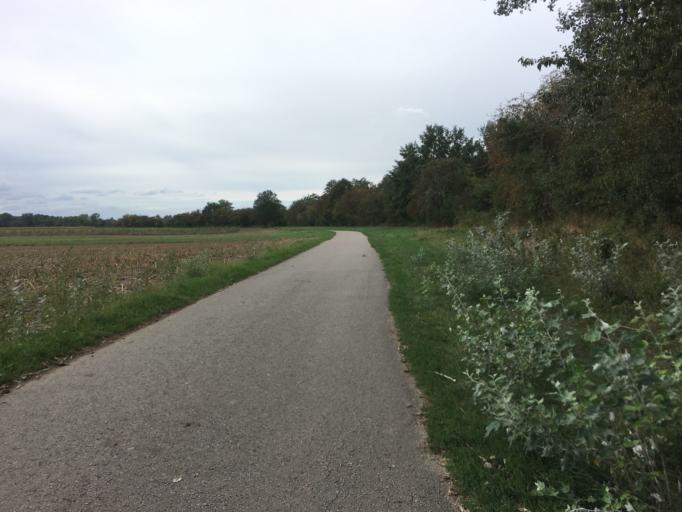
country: DE
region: Baden-Wuerttemberg
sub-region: Karlsruhe Region
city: Bruhl
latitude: 49.3971
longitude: 8.5259
